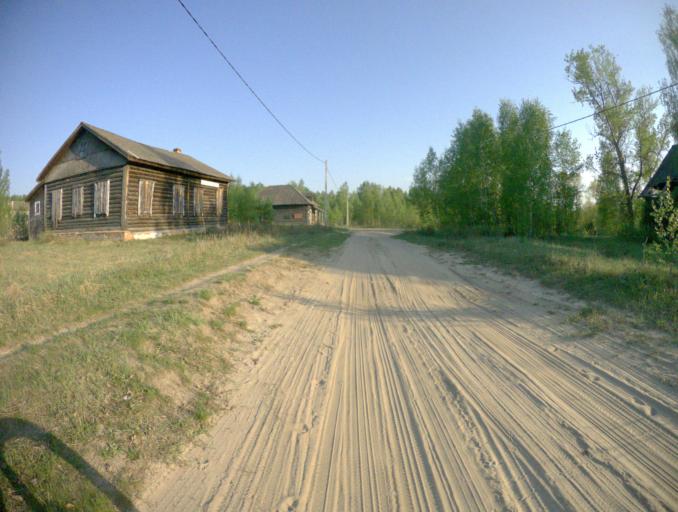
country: RU
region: Vladimir
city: Vyazniki
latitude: 56.3608
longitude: 42.1429
